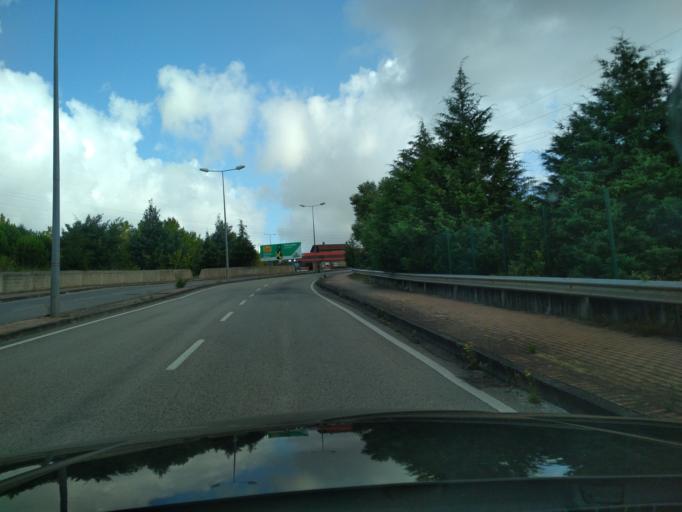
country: PT
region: Coimbra
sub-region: Coimbra
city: Coimbra
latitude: 40.1884
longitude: -8.4008
